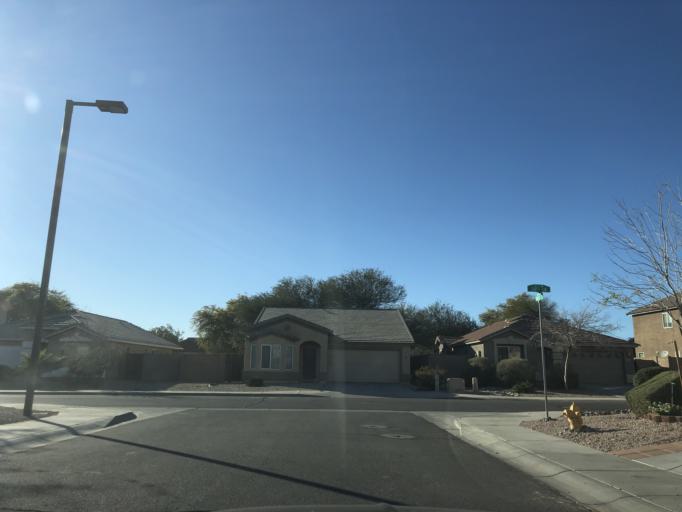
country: US
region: Arizona
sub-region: Maricopa County
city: Buckeye
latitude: 33.4379
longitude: -112.5708
